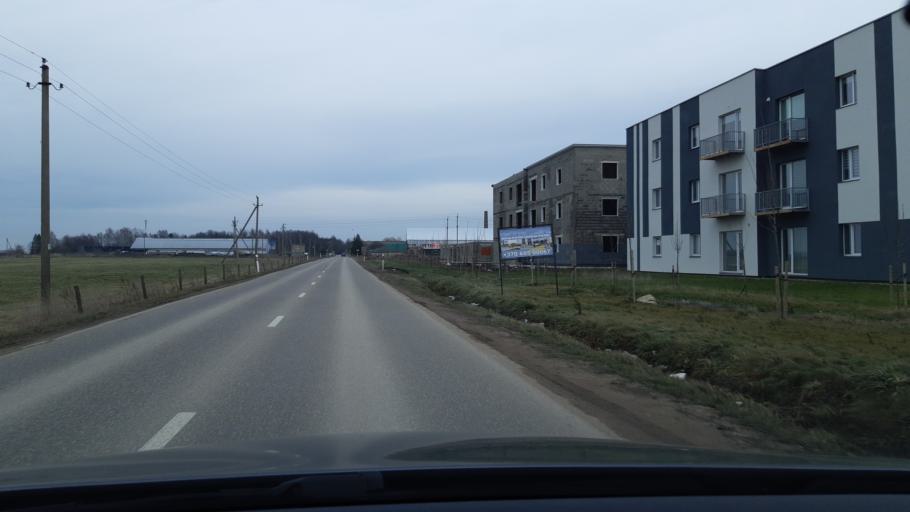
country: LT
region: Kauno apskritis
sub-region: Kaunas
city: Sargenai
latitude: 54.9535
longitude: 23.8547
